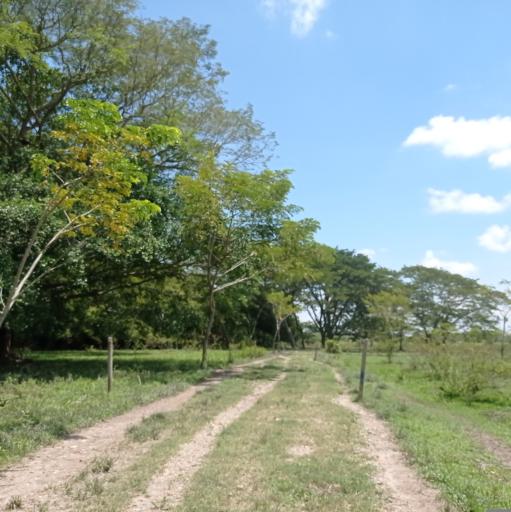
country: CO
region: Santander
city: Barrancabermeja
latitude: 7.1059
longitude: -73.8782
